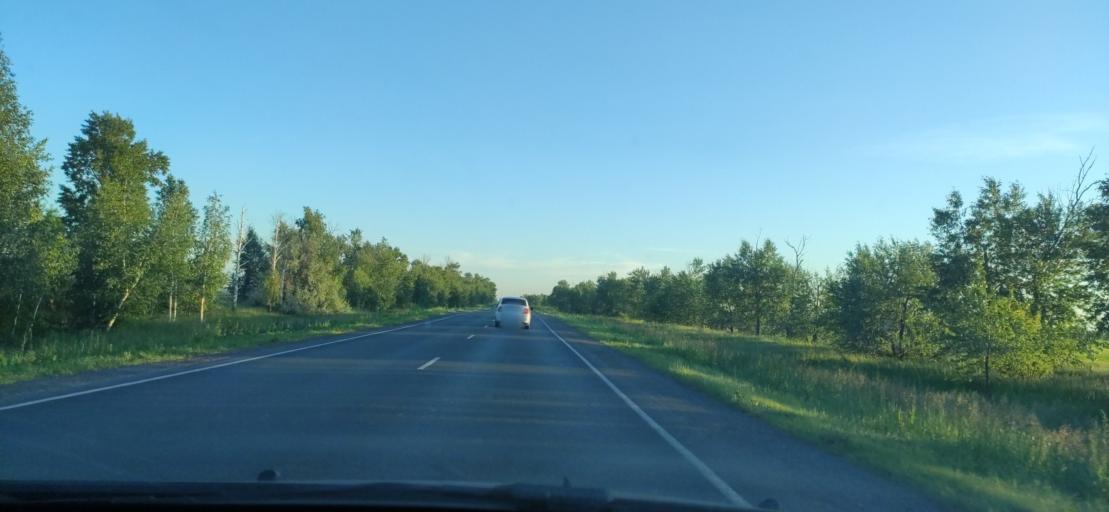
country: RU
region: Ulyanovsk
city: Cherdakly
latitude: 54.4021
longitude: 48.8639
